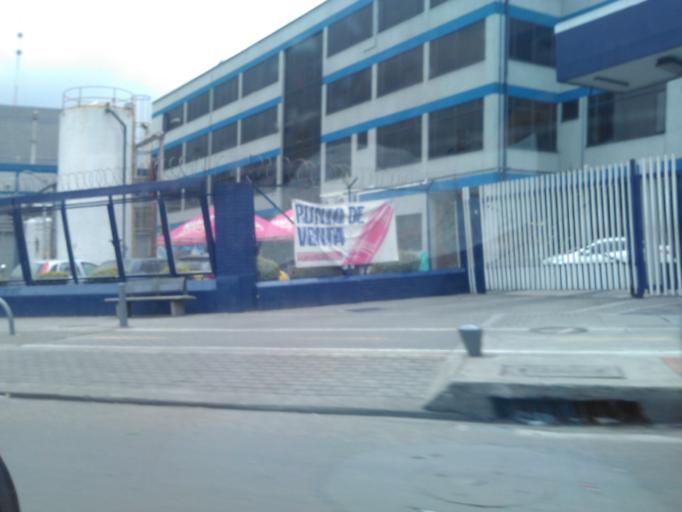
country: CO
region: Bogota D.C.
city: Bogota
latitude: 4.6274
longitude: -74.1098
